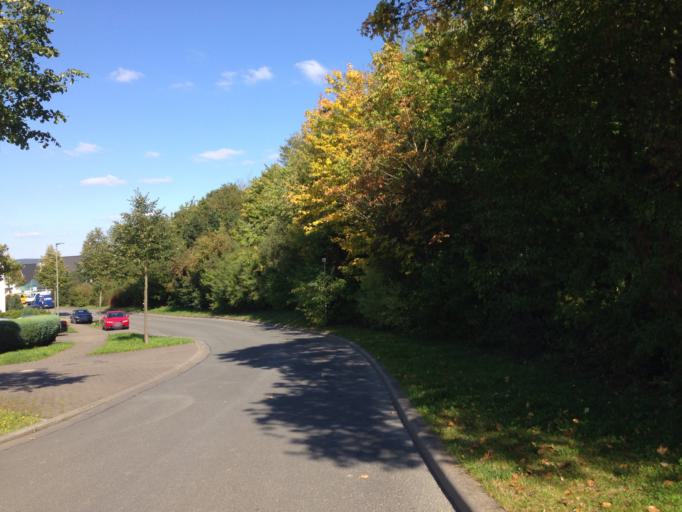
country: DE
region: Hesse
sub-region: Regierungsbezirk Giessen
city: Giessen
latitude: 50.6043
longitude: 8.6784
